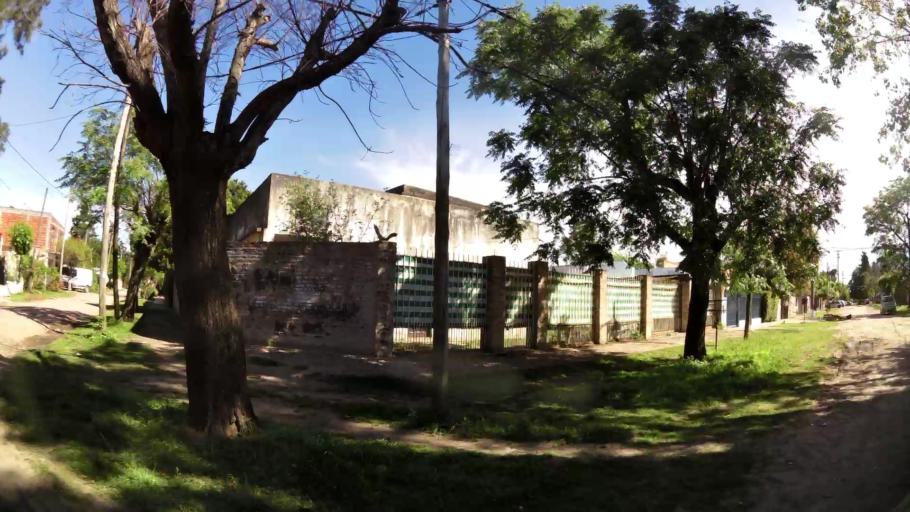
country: AR
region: Buenos Aires
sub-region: Partido de Almirante Brown
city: Adrogue
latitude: -34.7993
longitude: -58.3535
